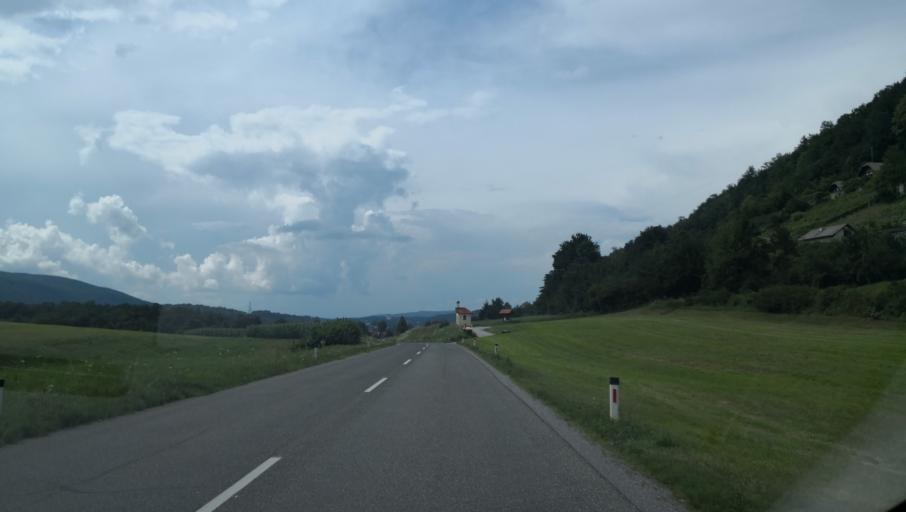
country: SI
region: Zuzemberk
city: Zuzemberk
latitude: 45.8028
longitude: 14.9747
